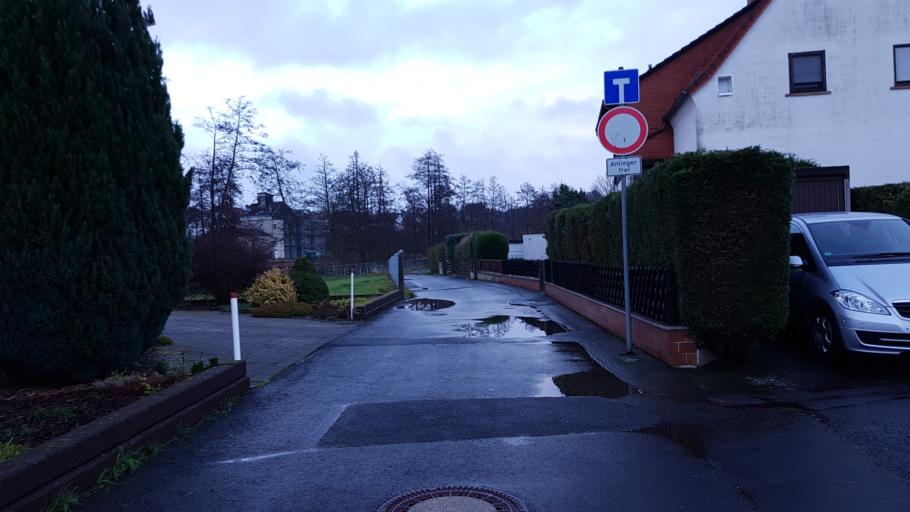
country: DE
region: Hesse
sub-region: Regierungsbezirk Giessen
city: Grunberg
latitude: 50.6449
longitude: 9.0327
